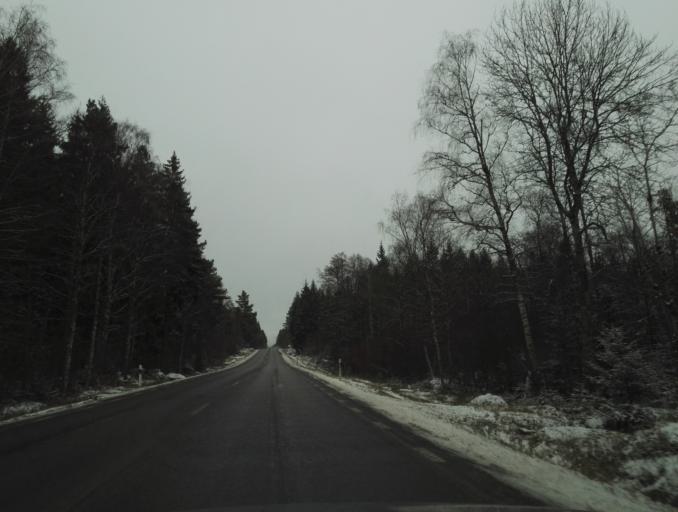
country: SE
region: Kronoberg
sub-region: Vaxjo Kommun
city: Gemla
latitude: 56.7838
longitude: 14.6055
